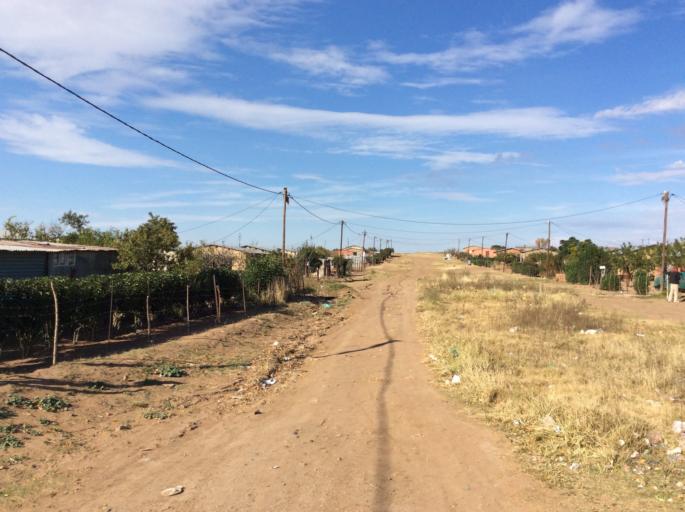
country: LS
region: Mafeteng
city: Mafeteng
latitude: -29.7146
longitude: 27.0146
